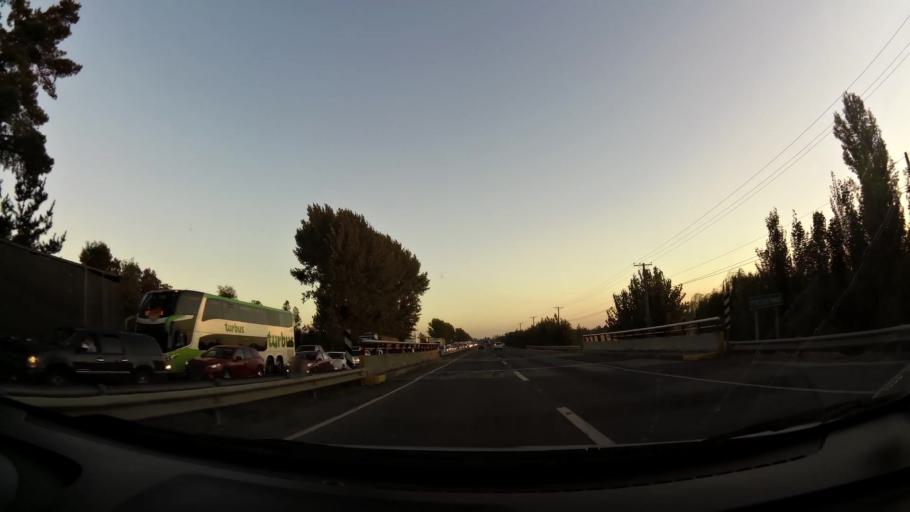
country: CL
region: Maule
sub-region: Provincia de Linares
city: Linares
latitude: -35.7535
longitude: -71.6728
